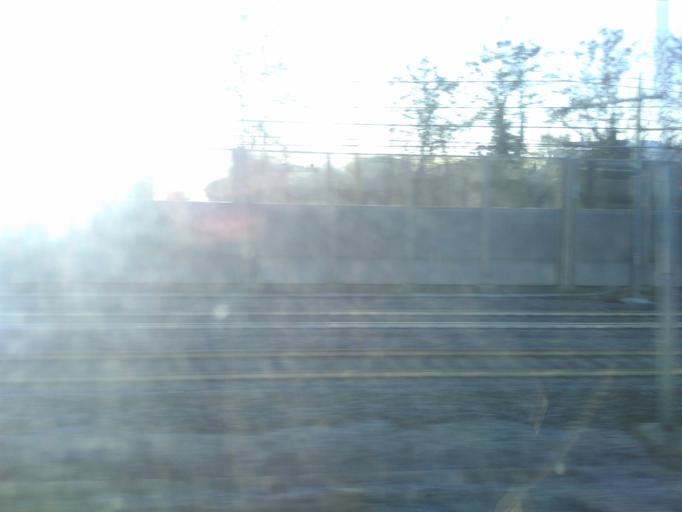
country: IT
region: Veneto
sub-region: Provincia di Padova
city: San Vito
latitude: 45.4309
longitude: 11.9560
